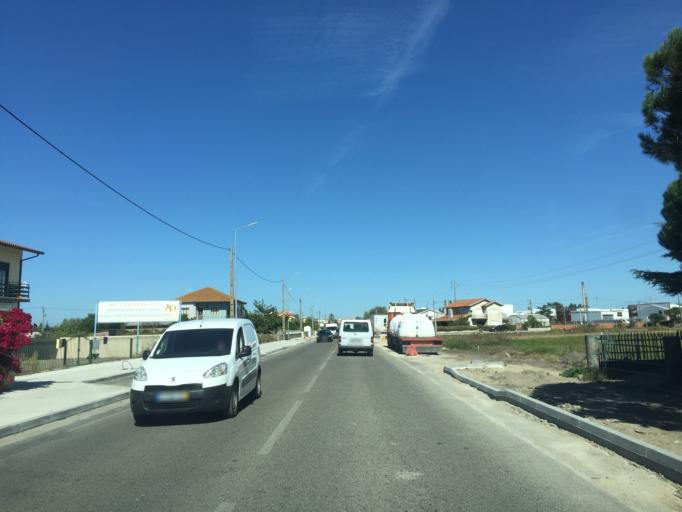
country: PT
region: Coimbra
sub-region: Montemor-O-Velho
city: Arazede
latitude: 40.3081
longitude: -8.7562
